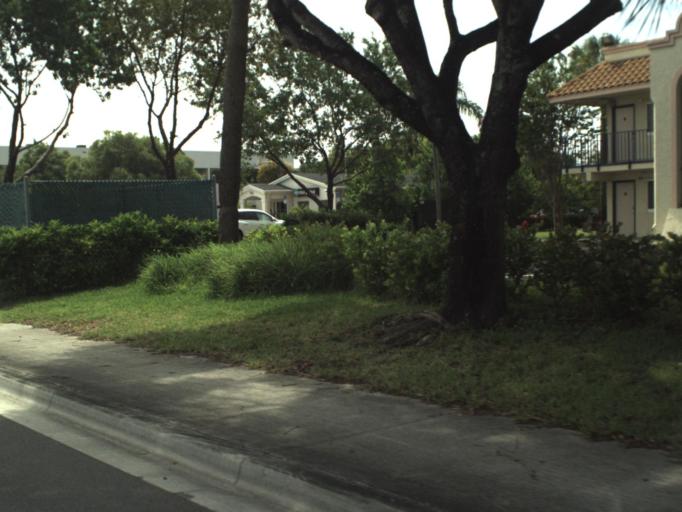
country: US
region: Florida
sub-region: Palm Beach County
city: Mangonia Park
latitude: 26.7830
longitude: -80.0938
